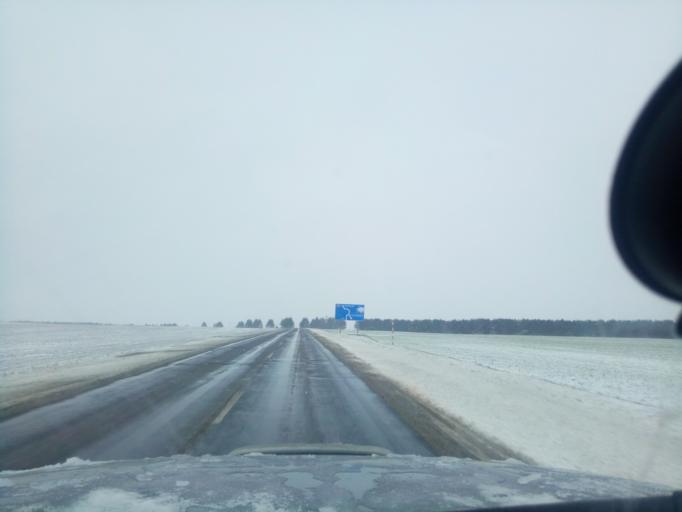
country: BY
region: Minsk
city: Haradzyeya
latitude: 53.2977
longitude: 26.5751
